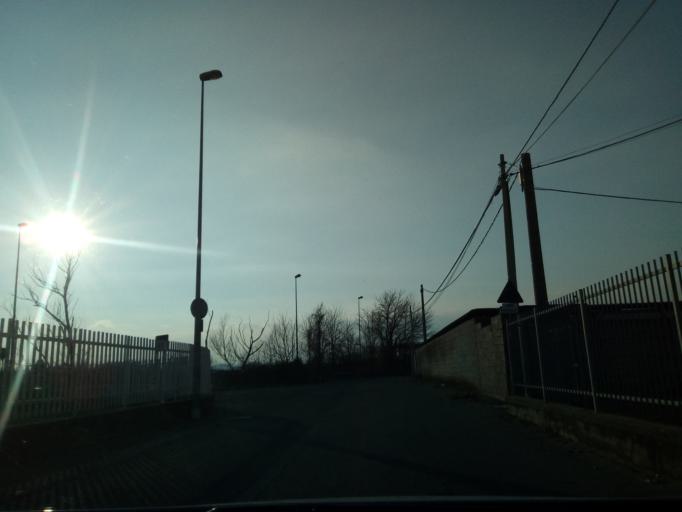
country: IT
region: Piedmont
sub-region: Provincia di Torino
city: Cascinette d'Ivrea
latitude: 45.4708
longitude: 7.9201
